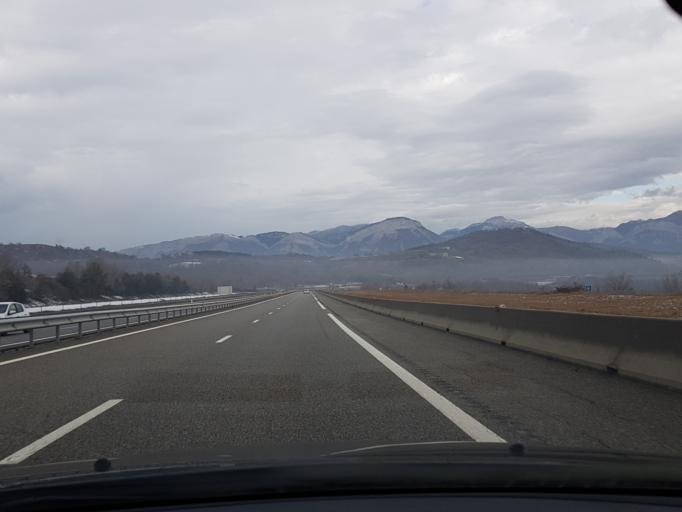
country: FR
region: Provence-Alpes-Cote d'Azur
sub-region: Departement des Hautes-Alpes
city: Laragne-Monteglin
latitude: 44.3138
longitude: 5.8969
